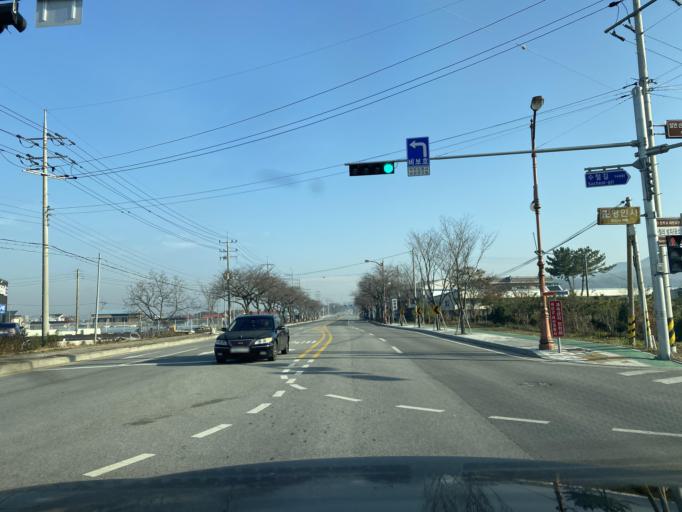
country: KR
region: Chungcheongnam-do
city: Yesan
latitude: 36.7181
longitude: 126.8449
